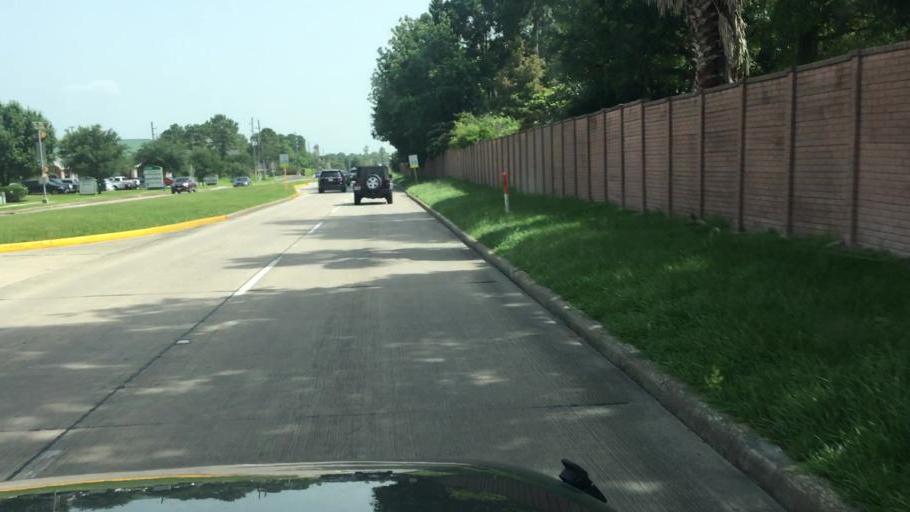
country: US
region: Texas
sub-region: Harris County
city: Atascocita
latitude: 29.9912
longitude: -95.1617
